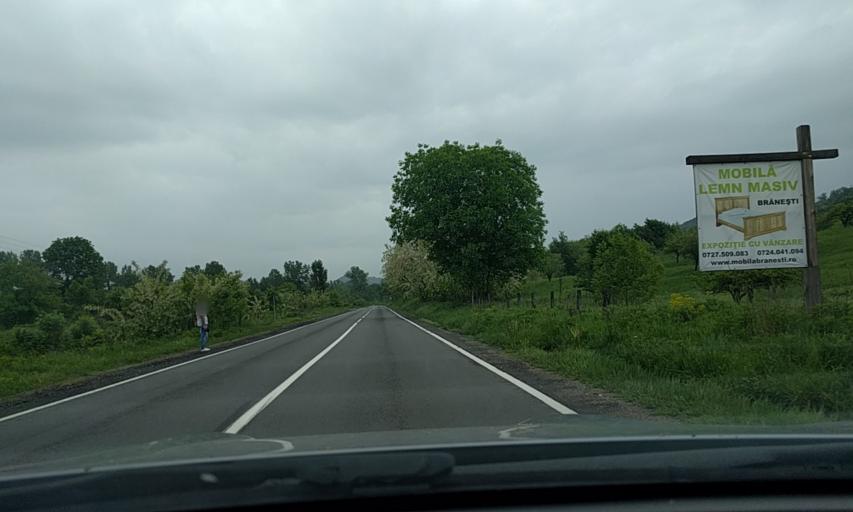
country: RO
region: Dambovita
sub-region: Comuna Branesti
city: Branesti
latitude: 45.0344
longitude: 25.4270
